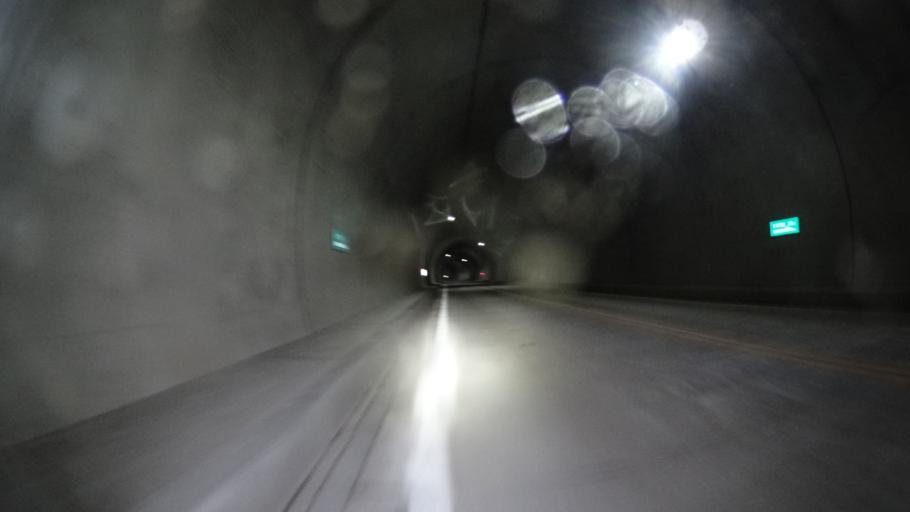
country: JP
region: Yamanashi
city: Enzan
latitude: 35.8018
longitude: 138.8649
